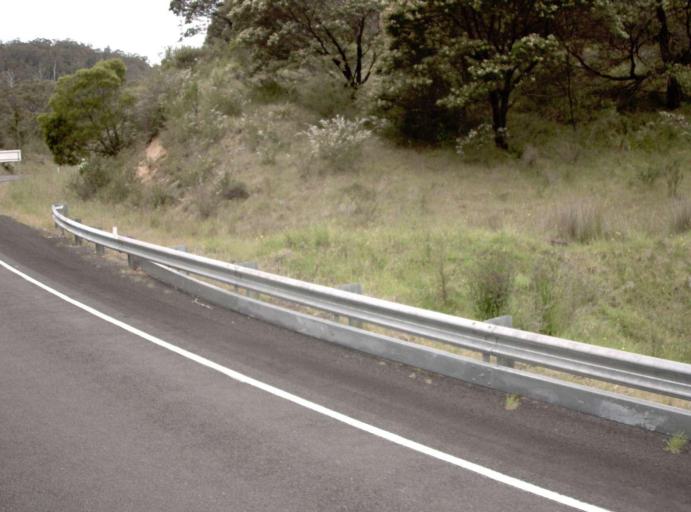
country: AU
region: New South Wales
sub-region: Bombala
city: Bombala
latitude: -37.2415
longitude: 149.2601
